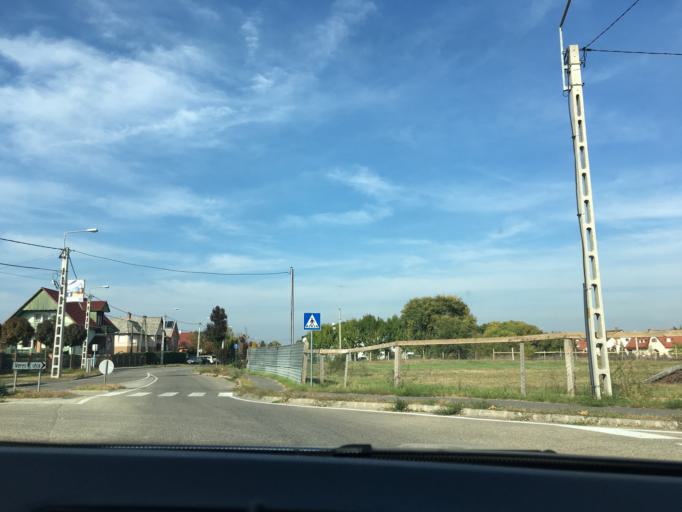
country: HU
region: Hajdu-Bihar
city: Debrecen
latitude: 47.5398
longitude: 21.6715
